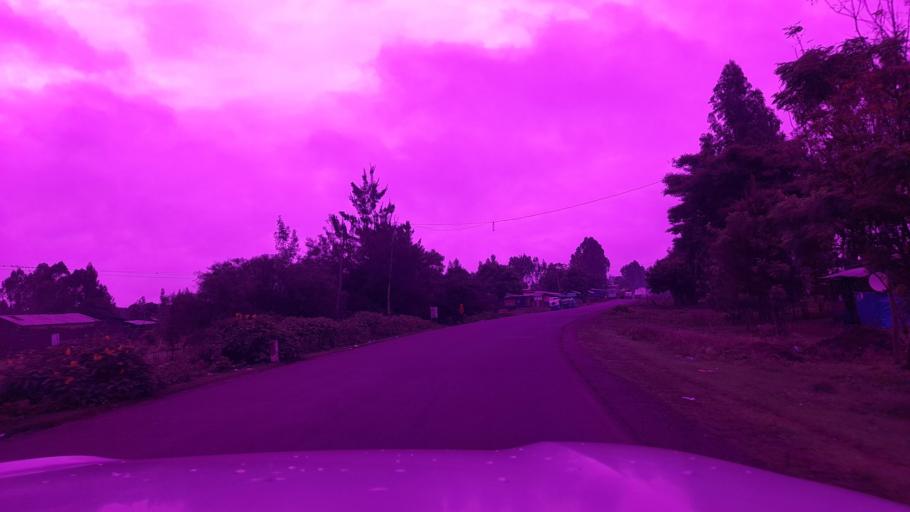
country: ET
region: Oromiya
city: Waliso
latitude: 8.2735
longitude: 37.6626
